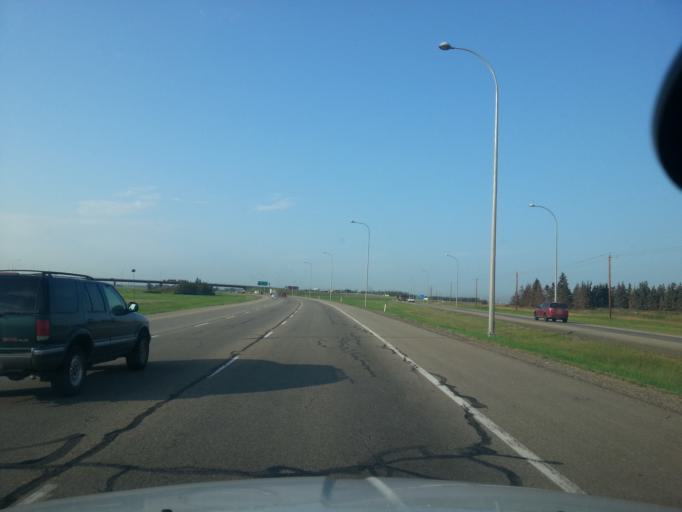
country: CA
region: Alberta
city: Leduc
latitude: 53.3436
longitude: -113.5479
